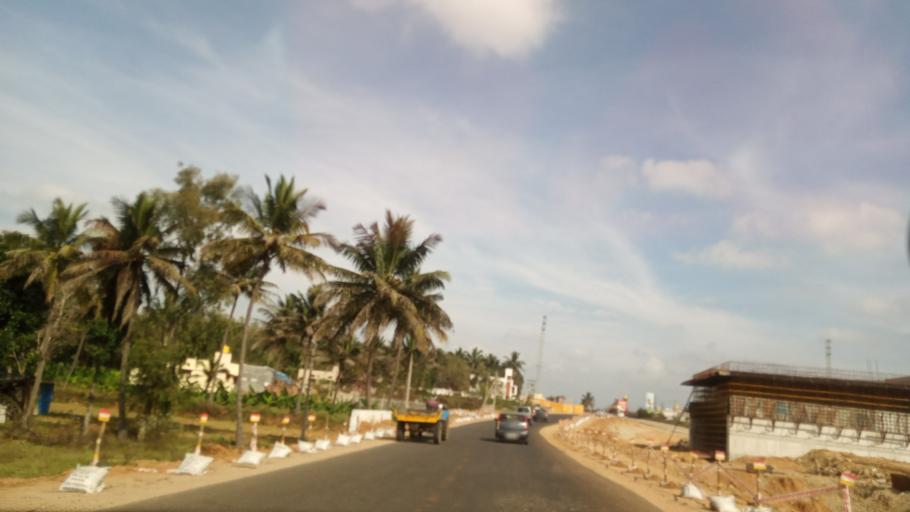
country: IN
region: Karnataka
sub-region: Mandya
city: Mandya
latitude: 12.4993
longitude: 76.8179
